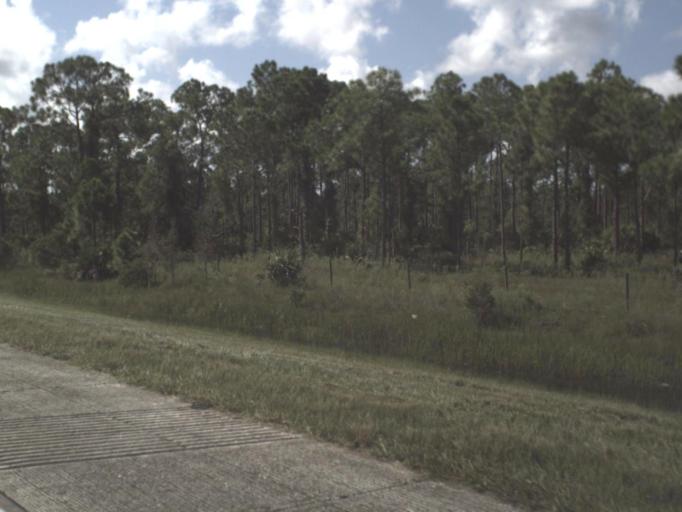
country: US
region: Florida
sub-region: Lee County
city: Burnt Store Marina
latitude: 26.8193
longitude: -81.9630
